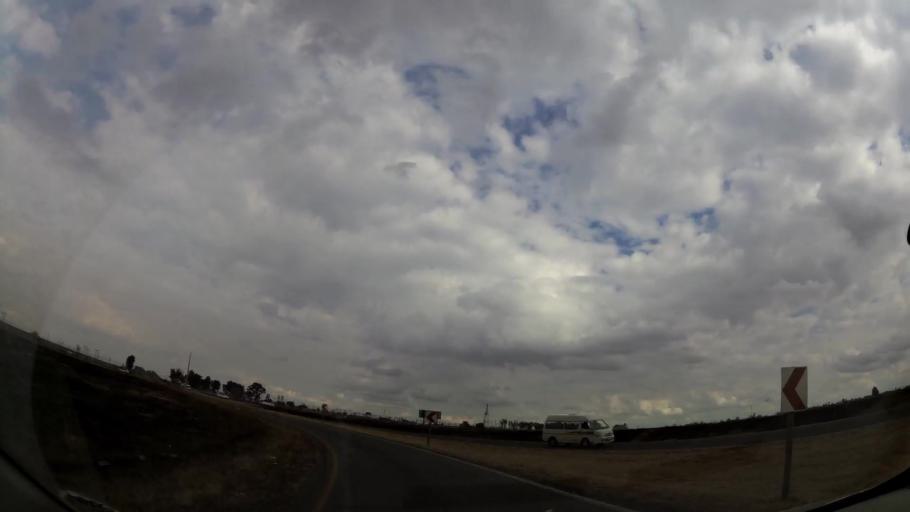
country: ZA
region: Orange Free State
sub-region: Fezile Dabi District Municipality
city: Sasolburg
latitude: -26.8405
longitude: 27.8720
